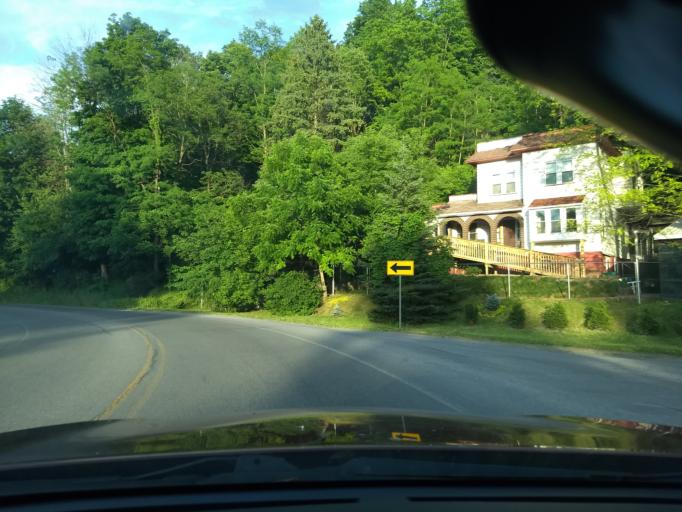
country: US
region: Pennsylvania
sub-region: Blair County
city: Lakemont
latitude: 40.4663
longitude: -78.4181
